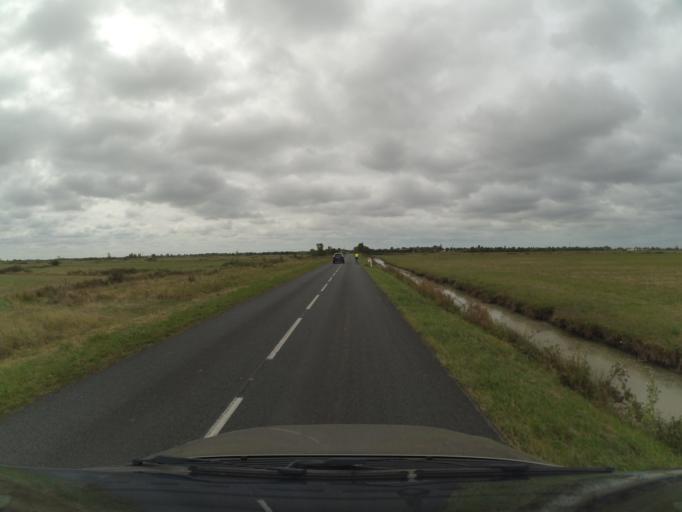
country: FR
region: Pays de la Loire
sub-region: Departement de la Vendee
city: Triaize
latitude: 46.4078
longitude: -1.2960
